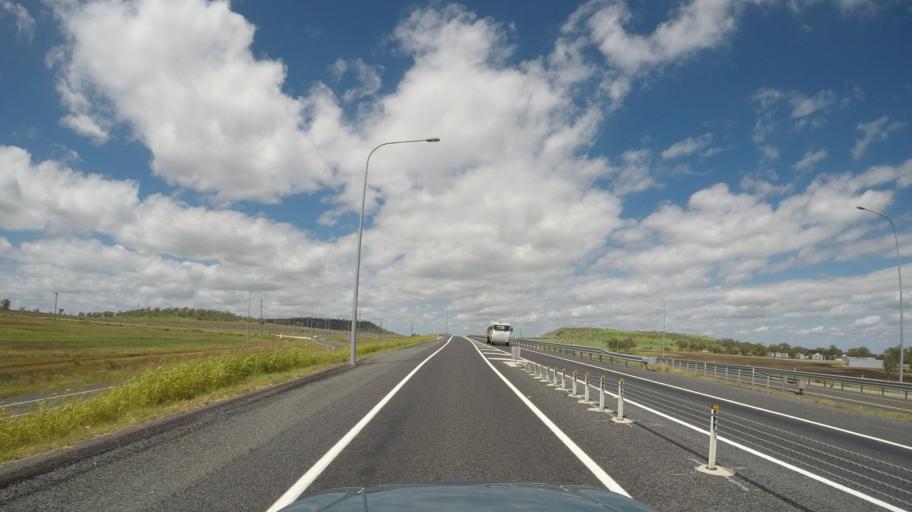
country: AU
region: Queensland
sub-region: Toowoomba
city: Westbrook
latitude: -27.5452
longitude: 151.8362
